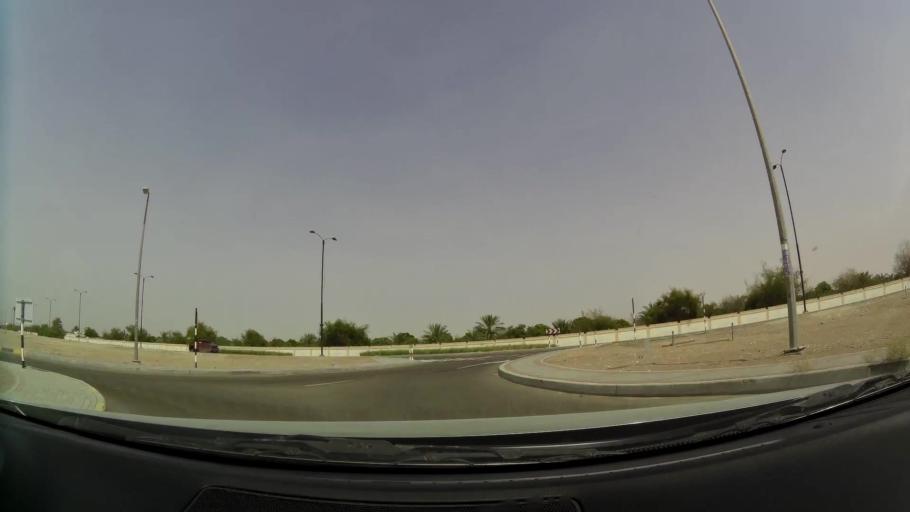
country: AE
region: Abu Dhabi
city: Al Ain
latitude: 24.1576
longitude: 55.6645
